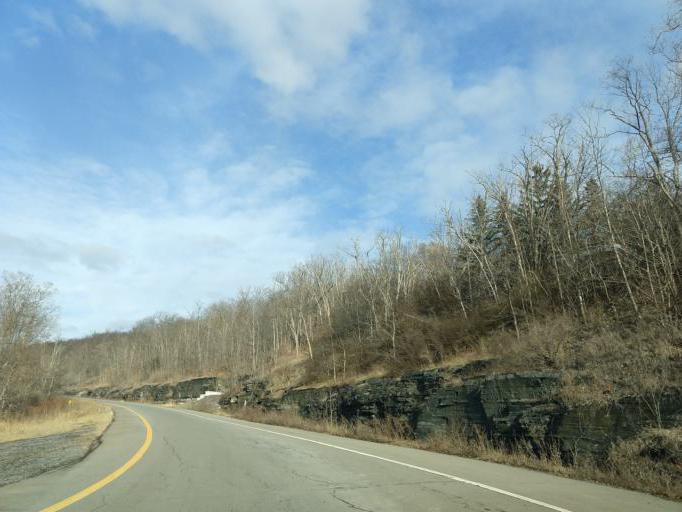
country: US
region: New York
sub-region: Tompkins County
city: Cayuga Heights
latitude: 42.4632
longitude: -76.4982
